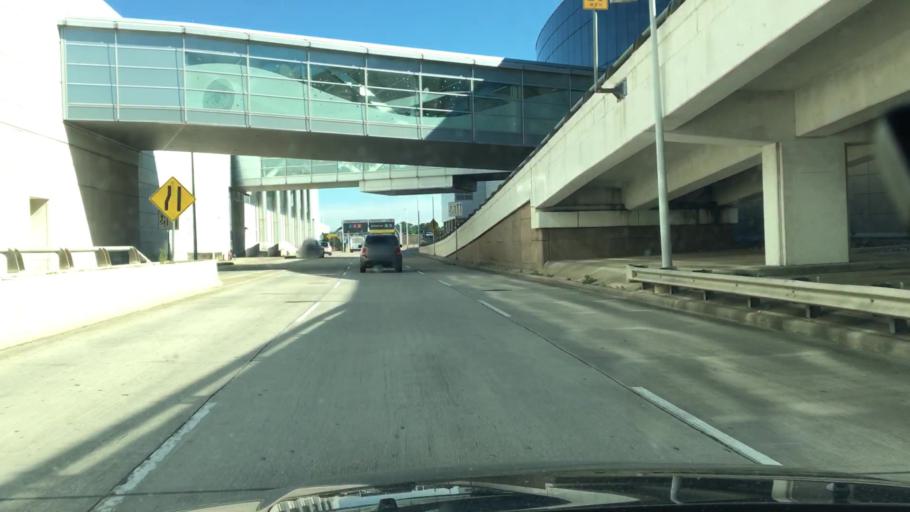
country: US
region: Texas
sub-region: Harris County
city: Aldine
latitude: 29.9859
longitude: -95.3341
